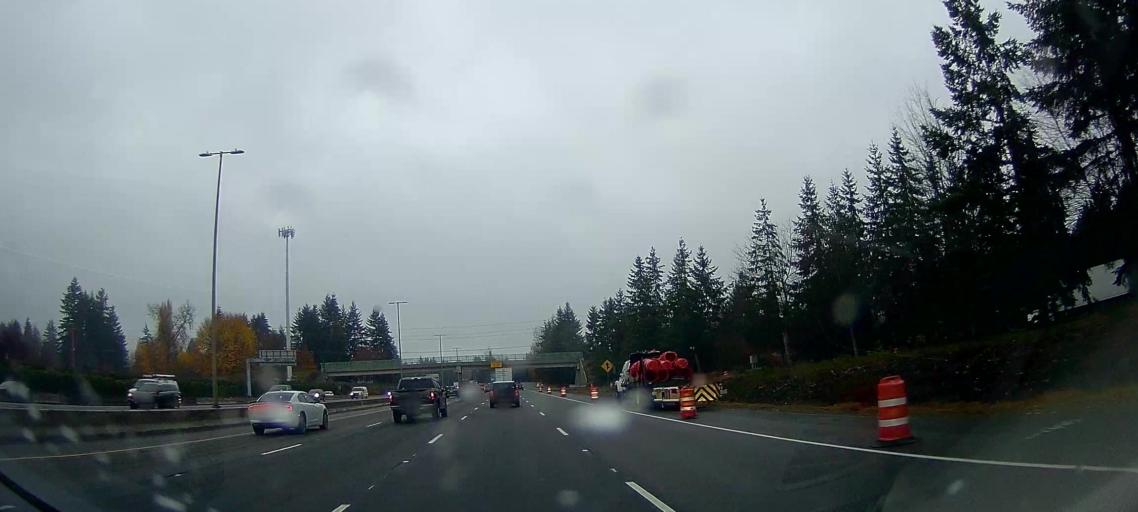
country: US
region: Washington
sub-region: Thurston County
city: Lacey
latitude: 47.0457
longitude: -122.8370
